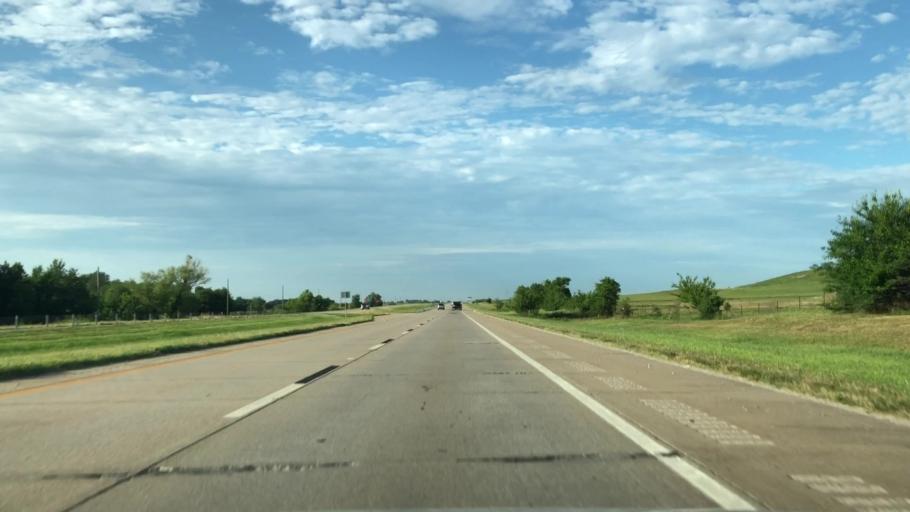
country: US
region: Oklahoma
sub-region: Osage County
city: Skiatook
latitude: 36.3960
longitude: -95.9206
